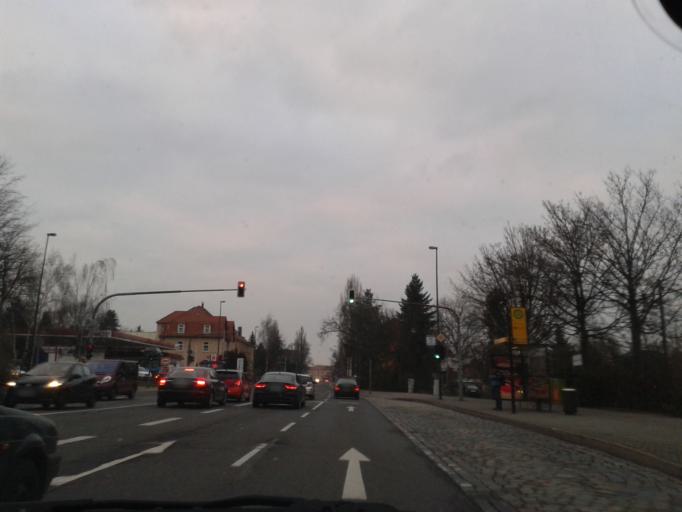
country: DE
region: Saxony
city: Dresden
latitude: 51.0154
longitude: 13.7719
